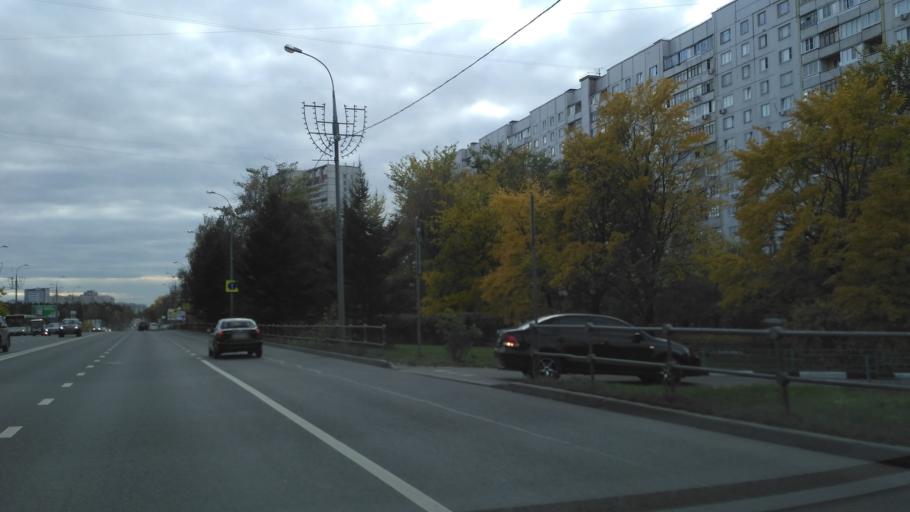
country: RU
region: Moscow
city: Zelenograd
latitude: 55.9969
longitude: 37.1910
